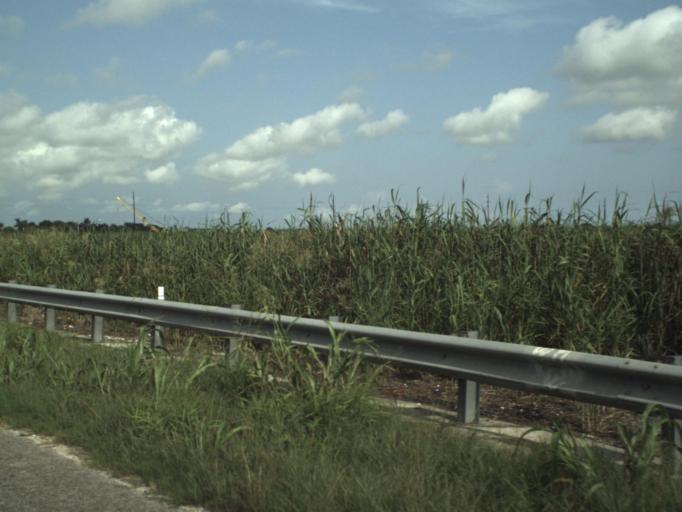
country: US
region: Florida
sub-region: Palm Beach County
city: South Bay
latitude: 26.6641
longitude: -80.7045
